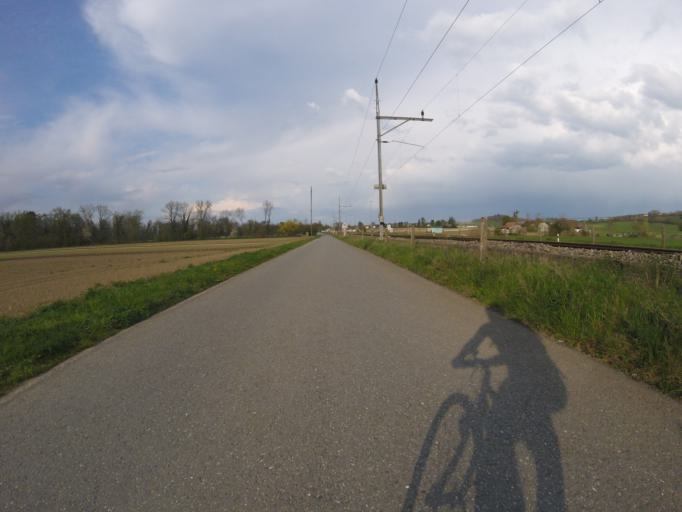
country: CH
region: Fribourg
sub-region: See District
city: Gurwolf
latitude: 46.9160
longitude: 7.0917
